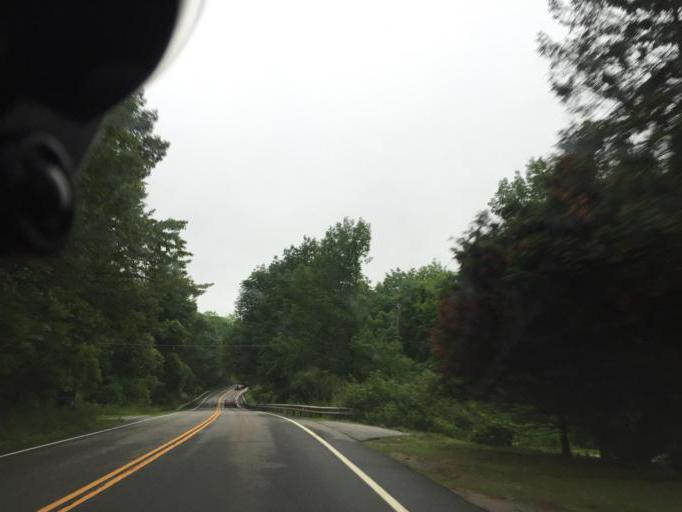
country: US
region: Connecticut
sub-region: Litchfield County
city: Canaan
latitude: 41.9046
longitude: -73.2719
